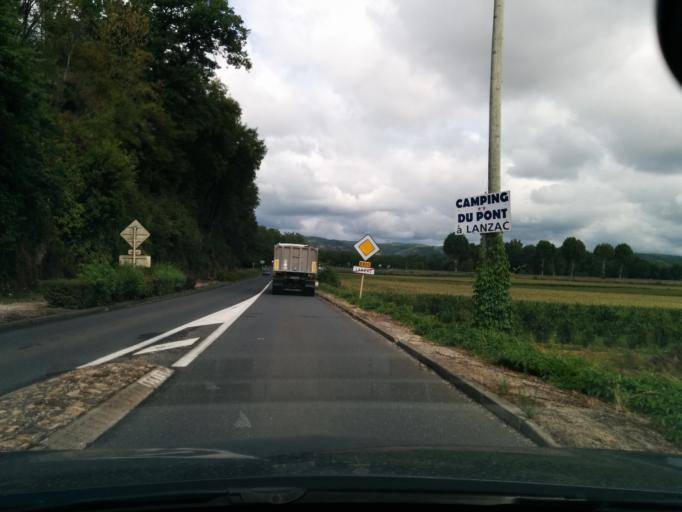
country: FR
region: Midi-Pyrenees
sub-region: Departement du Lot
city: Souillac
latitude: 44.8779
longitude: 1.4837
